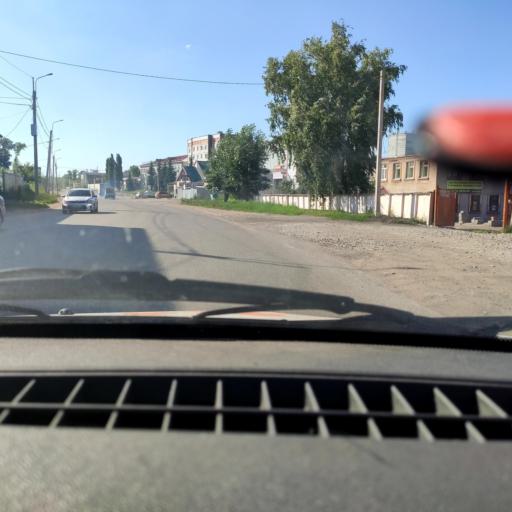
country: RU
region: Bashkortostan
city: Sterlitamak
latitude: 53.6505
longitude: 55.9778
